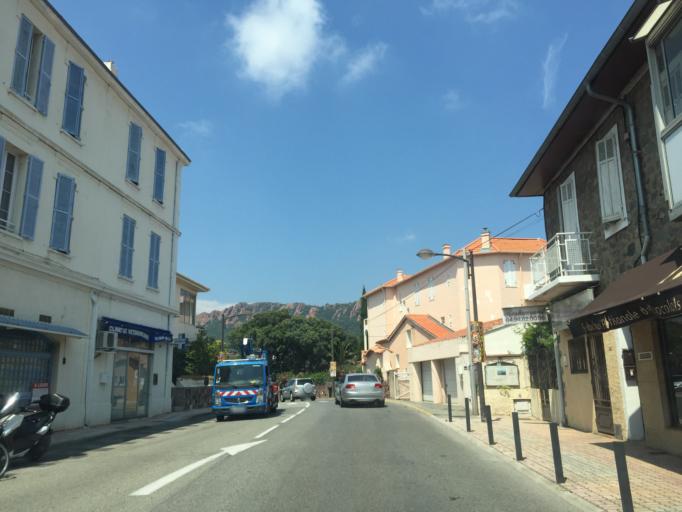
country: FR
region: Provence-Alpes-Cote d'Azur
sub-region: Departement du Var
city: Saint-Raphael
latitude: 43.4293
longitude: 6.8565
